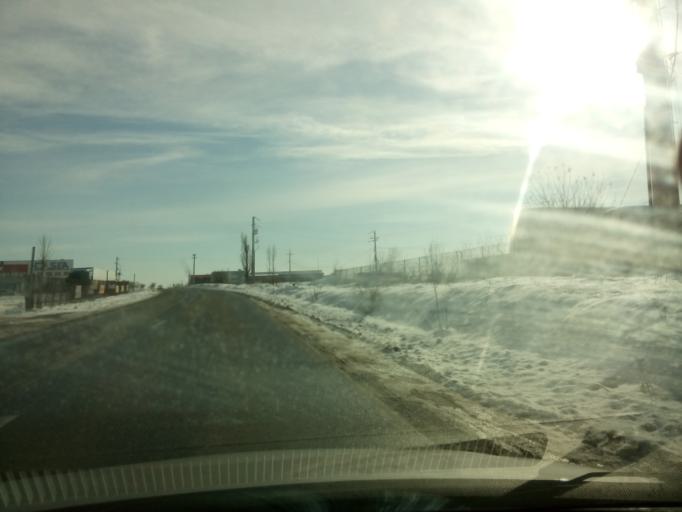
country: RO
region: Ilfov
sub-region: Comuna Popesti-Leordeni
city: Popesti-Leordeni
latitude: 44.3676
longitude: 26.1863
